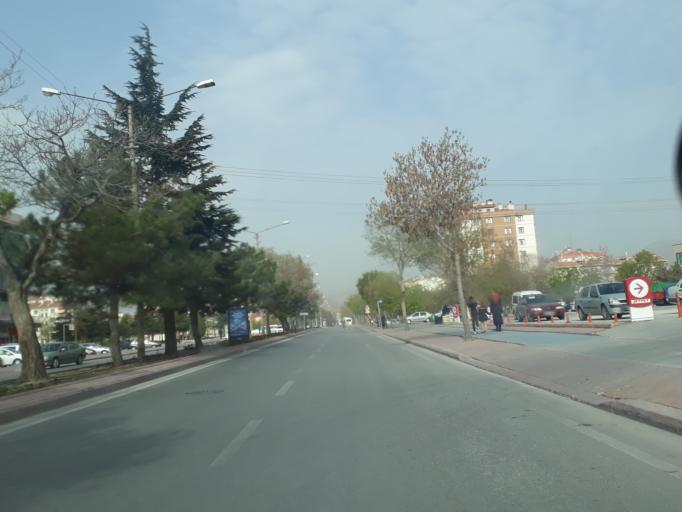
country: TR
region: Konya
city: Selcuklu
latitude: 37.9372
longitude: 32.5017
